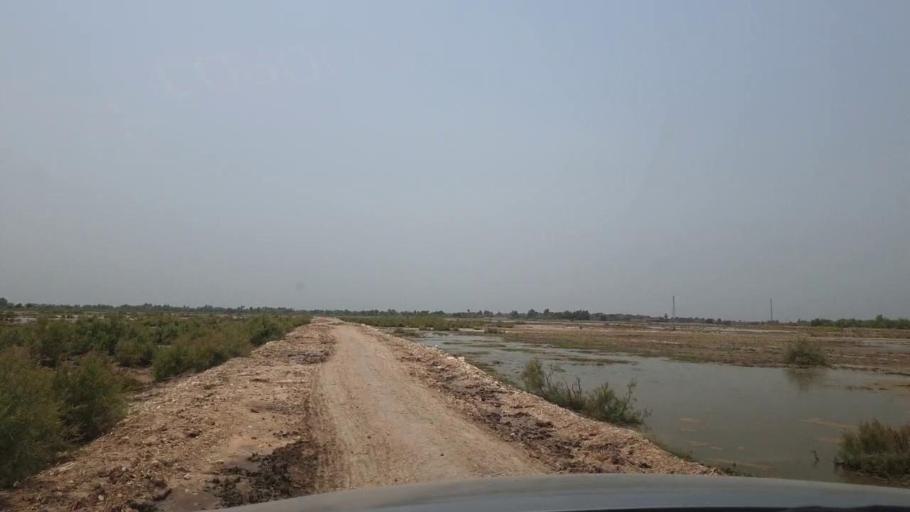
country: PK
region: Sindh
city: Garhi Yasin
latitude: 27.8599
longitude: 68.4786
